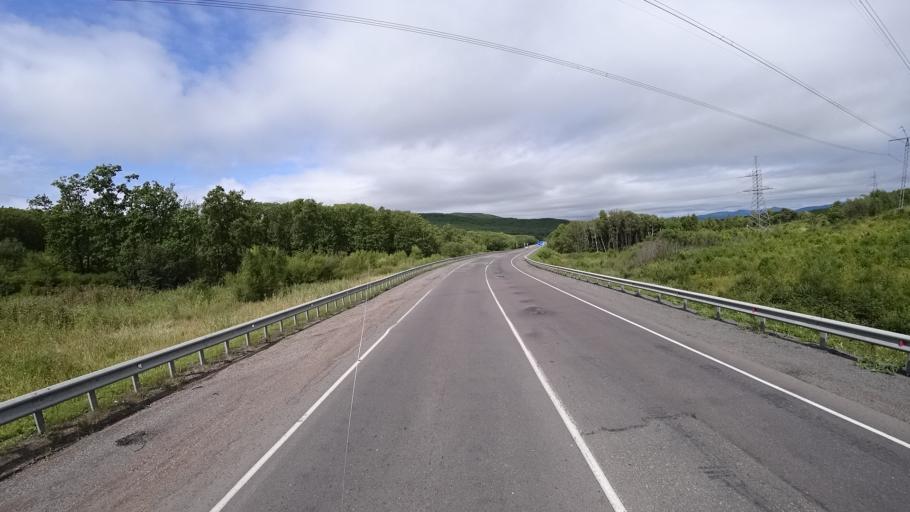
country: RU
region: Primorskiy
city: Lyalichi
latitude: 44.1331
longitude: 132.4273
